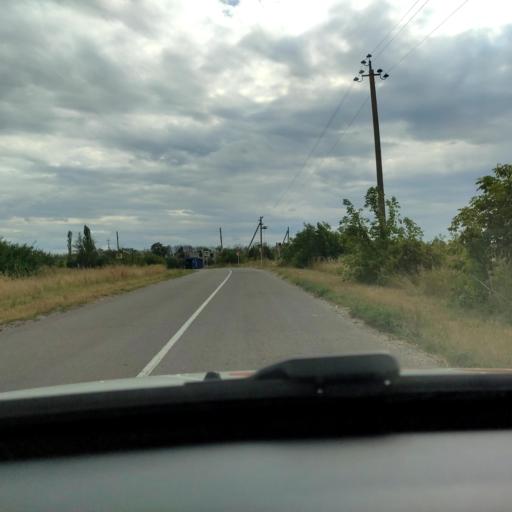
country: RU
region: Voronezj
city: Orlovo
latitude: 51.6623
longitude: 39.5724
